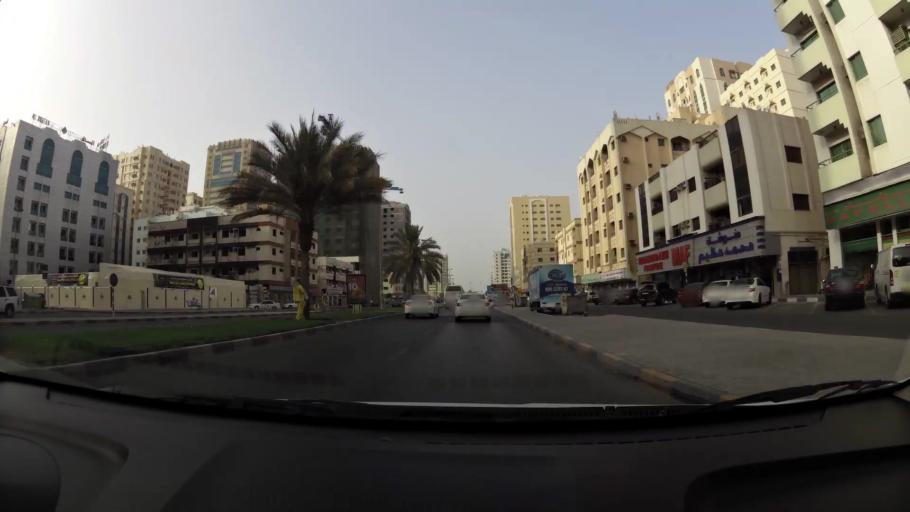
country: AE
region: Ash Shariqah
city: Sharjah
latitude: 25.3410
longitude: 55.3945
